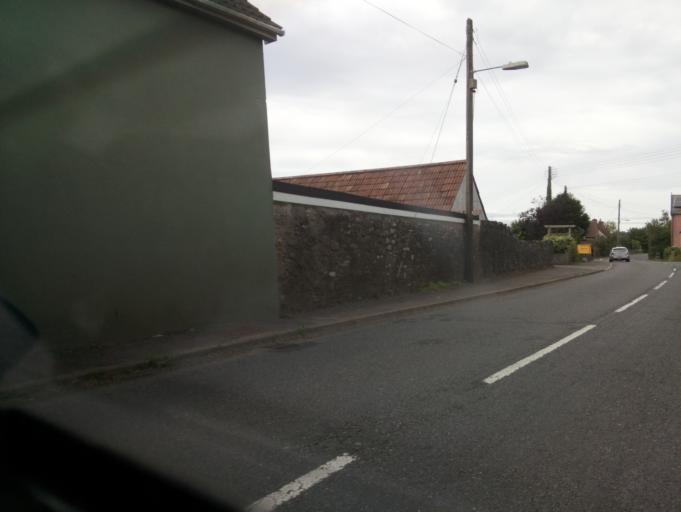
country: GB
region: England
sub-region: Somerset
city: Wells
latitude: 51.2268
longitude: -2.7003
